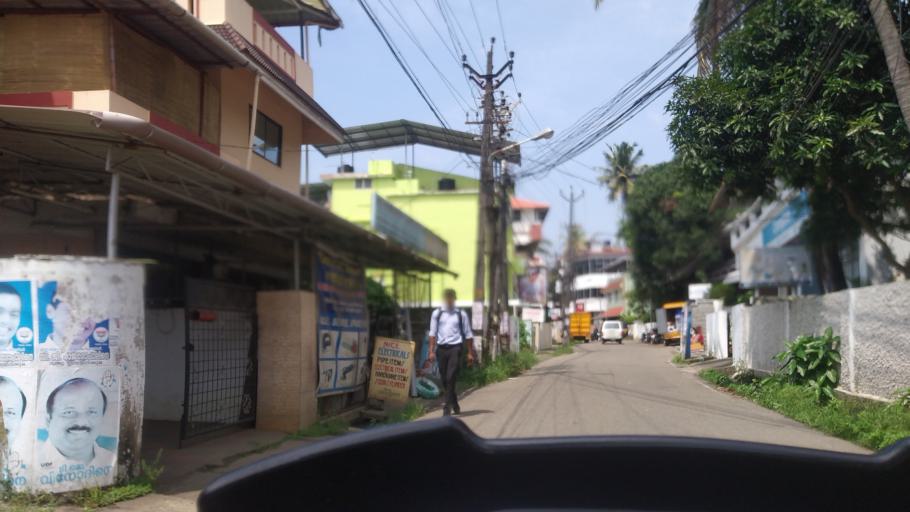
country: IN
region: Kerala
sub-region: Ernakulam
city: Cochin
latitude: 9.9899
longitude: 76.2972
